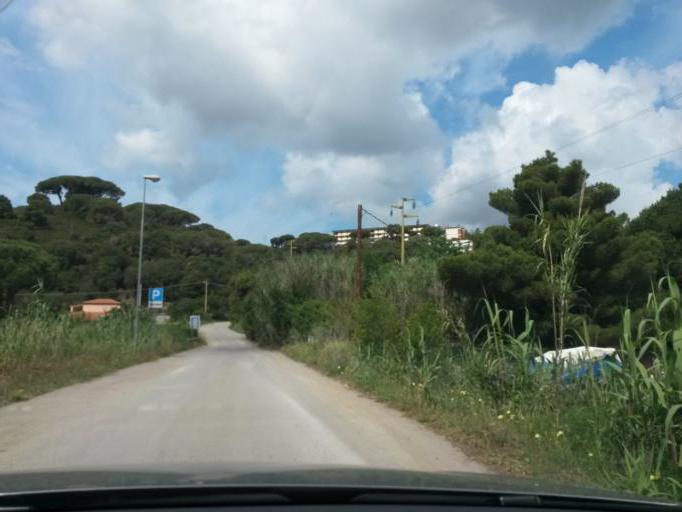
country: IT
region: Tuscany
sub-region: Provincia di Livorno
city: Porto Azzurro
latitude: 42.7549
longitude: 10.3994
